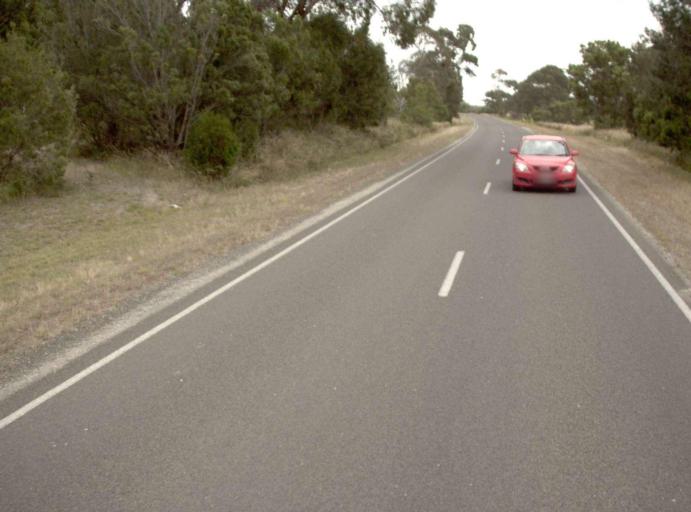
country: AU
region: Victoria
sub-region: Wellington
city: Sale
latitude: -38.1949
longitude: 147.2902
